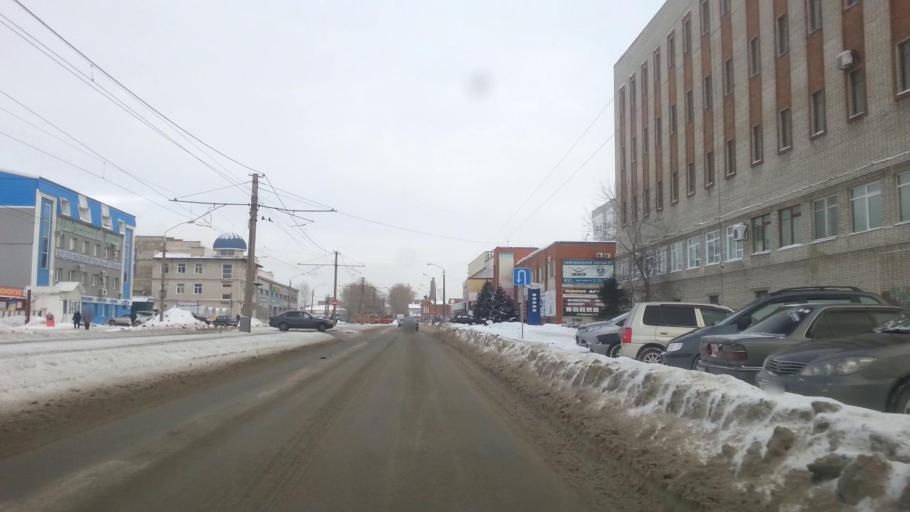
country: RU
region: Altai Krai
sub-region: Gorod Barnaulskiy
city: Barnaul
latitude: 53.3741
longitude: 83.7521
